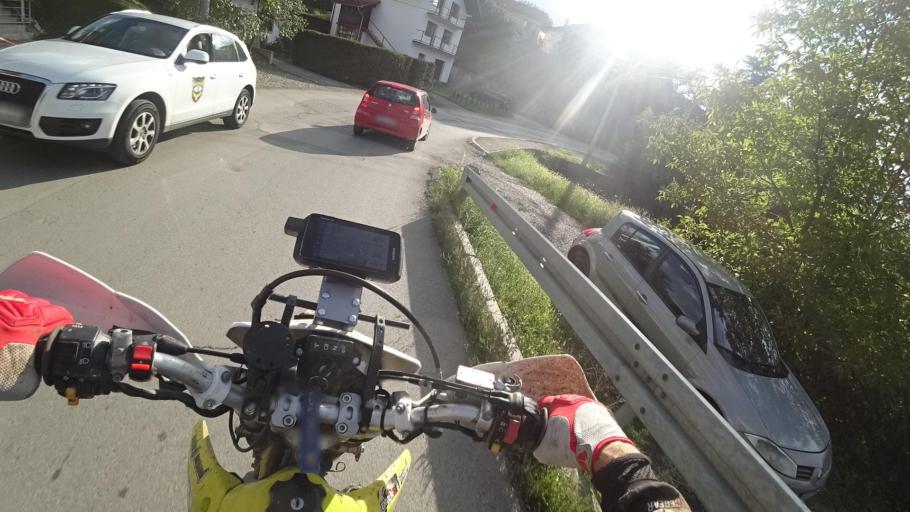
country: BA
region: Republika Srpska
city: Starcevica
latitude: 44.7546
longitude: 17.2187
